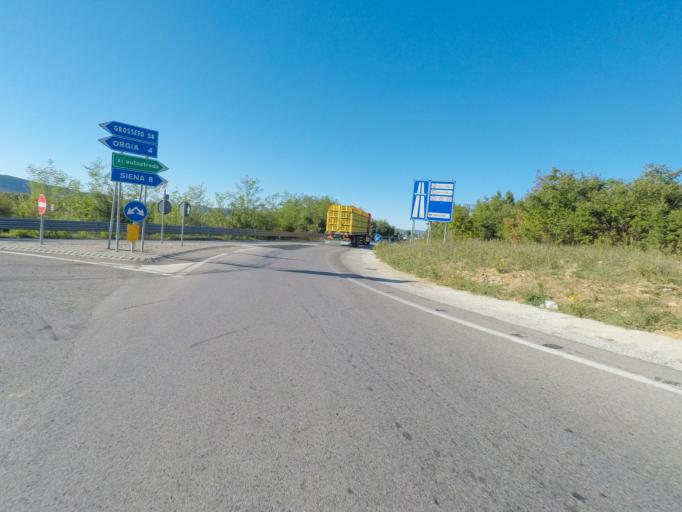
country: IT
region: Tuscany
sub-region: Provincia di Siena
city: Rosia
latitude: 43.2197
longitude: 11.2749
